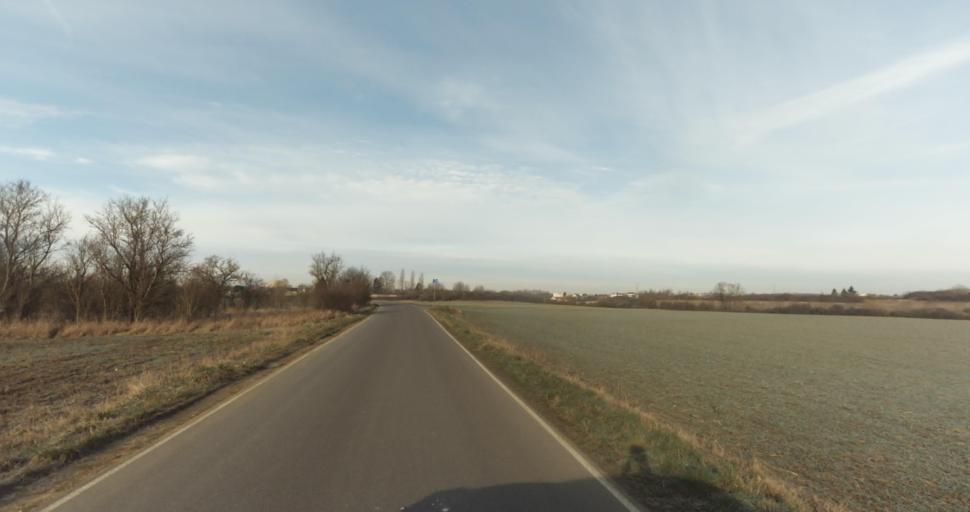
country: FR
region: Lorraine
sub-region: Departement de Meurthe-et-Moselle
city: Giraumont
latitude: 49.1598
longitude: 5.8983
